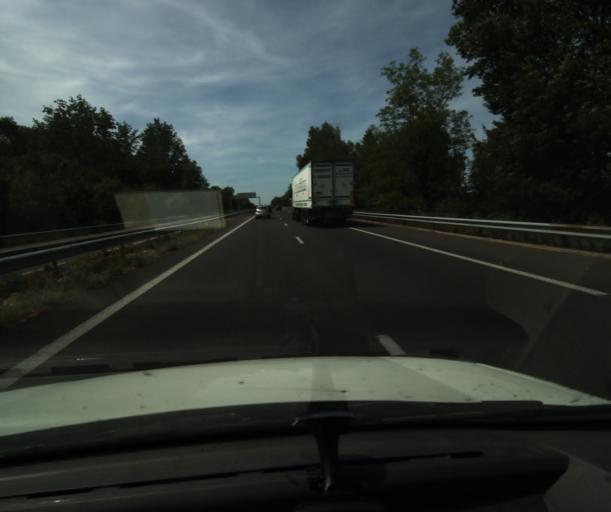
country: FR
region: Languedoc-Roussillon
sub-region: Departement de l'Aude
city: Villeneuve-la-Comptal
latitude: 43.2993
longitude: 1.9242
